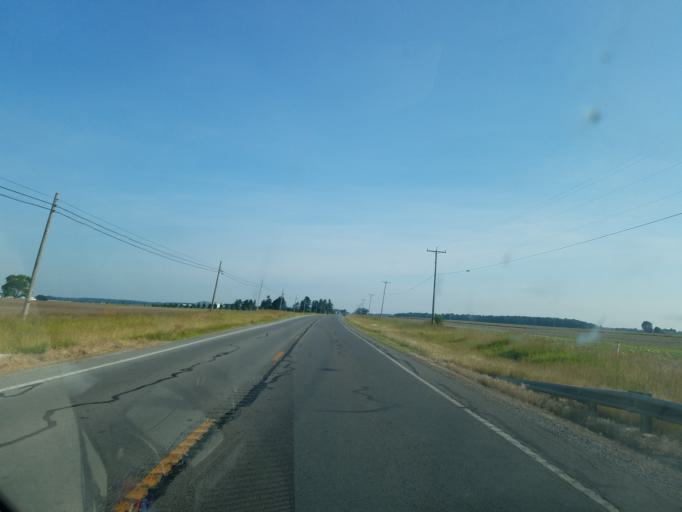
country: US
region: Ohio
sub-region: Hardin County
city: Kenton
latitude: 40.6771
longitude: -83.6132
